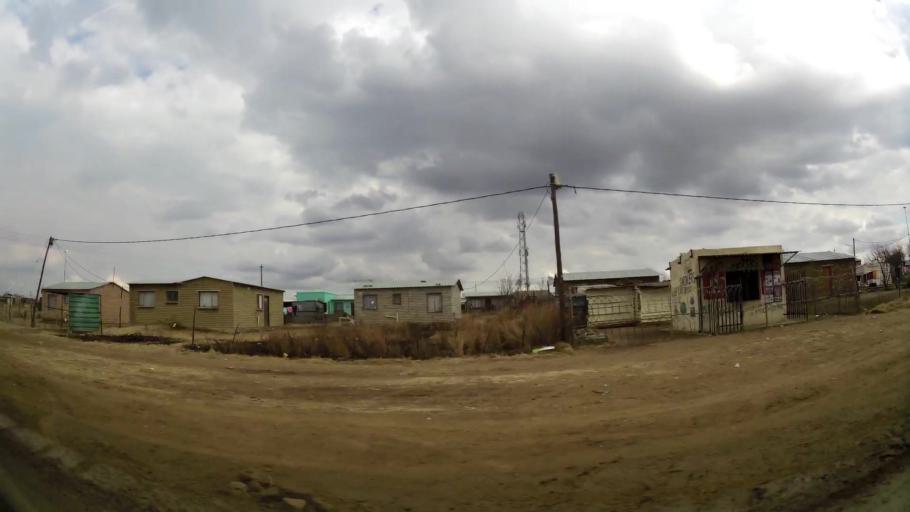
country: ZA
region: Orange Free State
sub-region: Fezile Dabi District Municipality
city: Sasolburg
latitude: -26.8779
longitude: 27.8751
